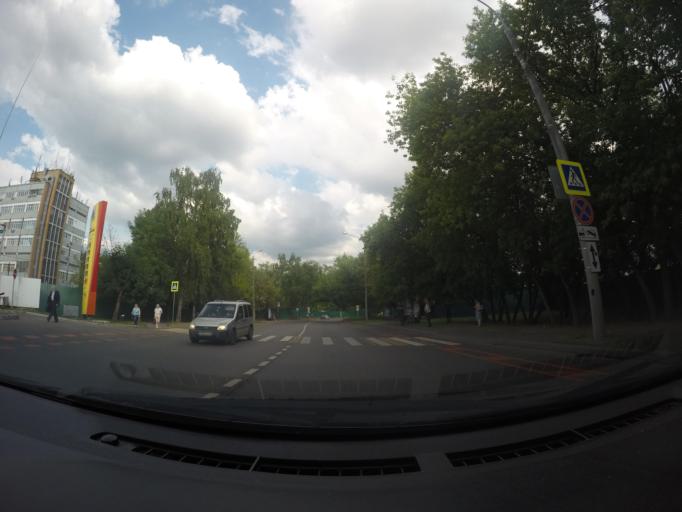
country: RU
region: Moscow
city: Kozeyevo
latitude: 55.8582
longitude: 37.6234
